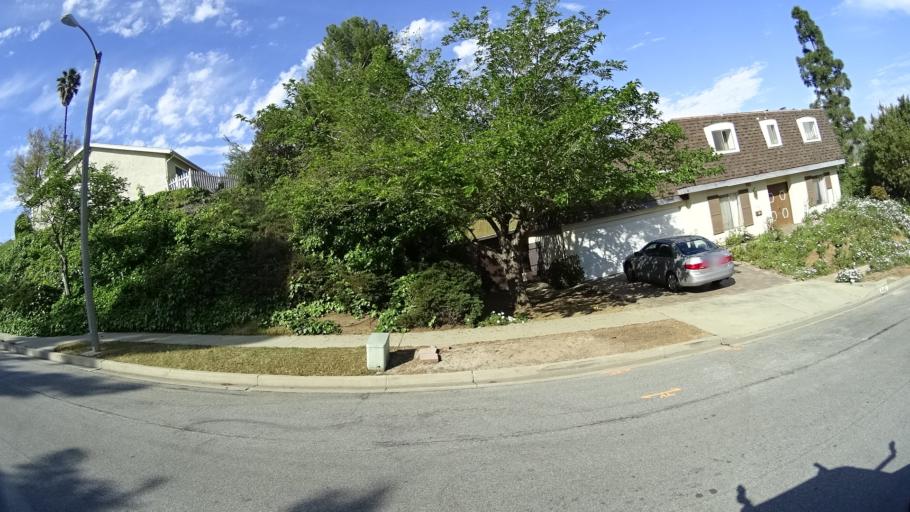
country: US
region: California
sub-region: Ventura County
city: Casa Conejo
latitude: 34.1757
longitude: -118.9422
